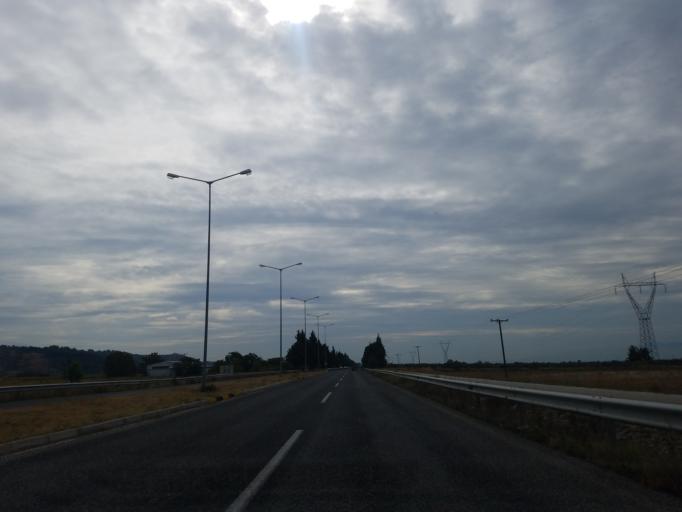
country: GR
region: Thessaly
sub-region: Trikala
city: Vasiliki
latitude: 39.6532
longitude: 21.6818
